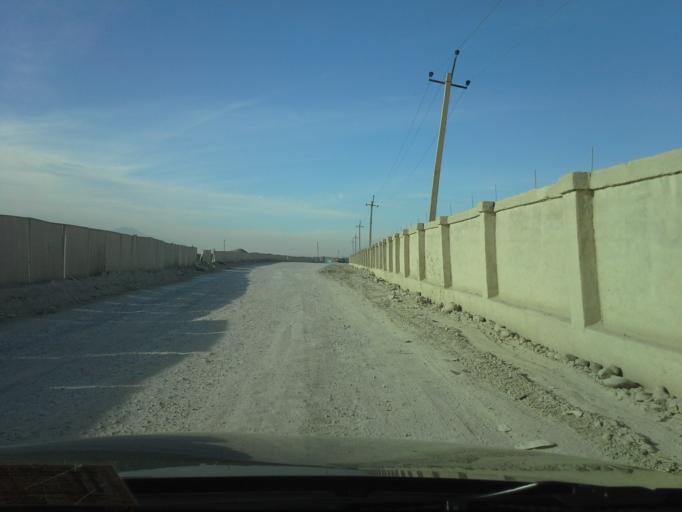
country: TM
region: Ahal
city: Abadan
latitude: 38.0300
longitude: 58.1615
